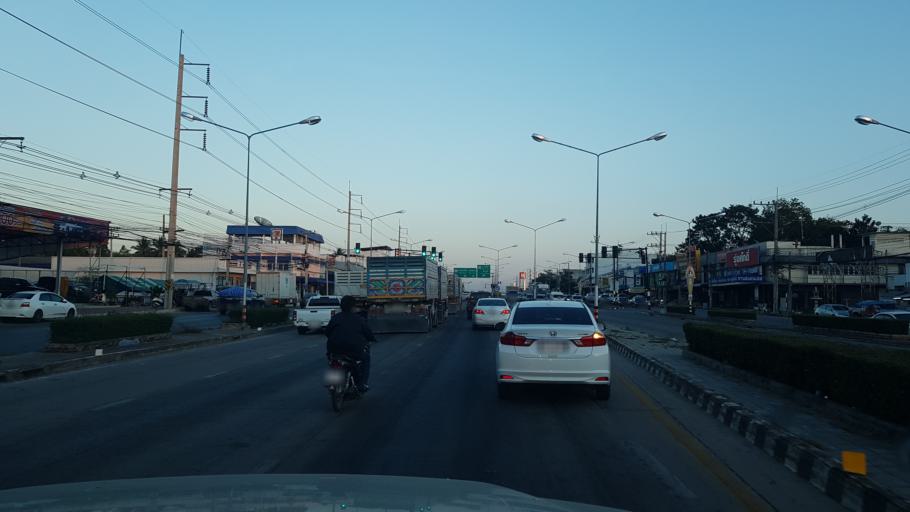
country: TH
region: Khon Kaen
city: Chum Phae
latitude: 16.5427
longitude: 102.1048
